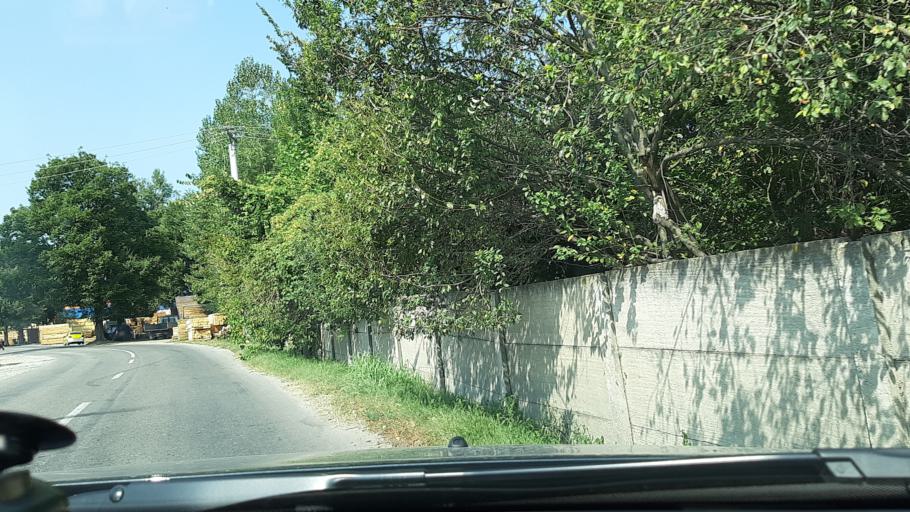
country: RO
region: Gorj
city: Targu Jiu
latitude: 45.0168
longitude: 23.2644
